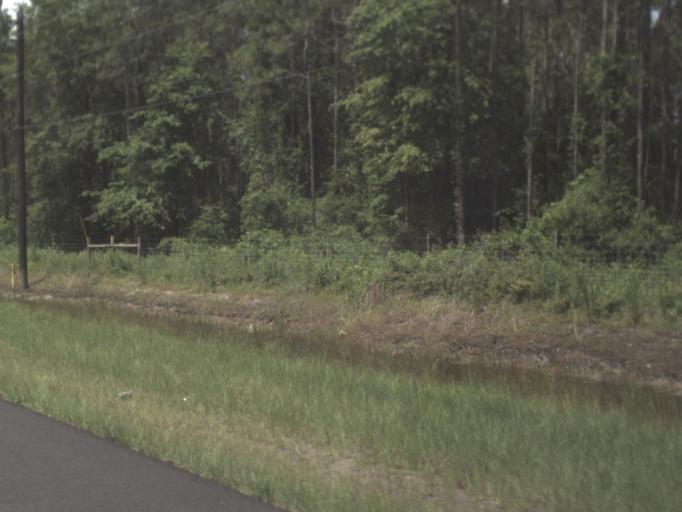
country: US
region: Florida
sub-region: Duval County
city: Baldwin
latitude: 30.4143
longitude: -81.9298
